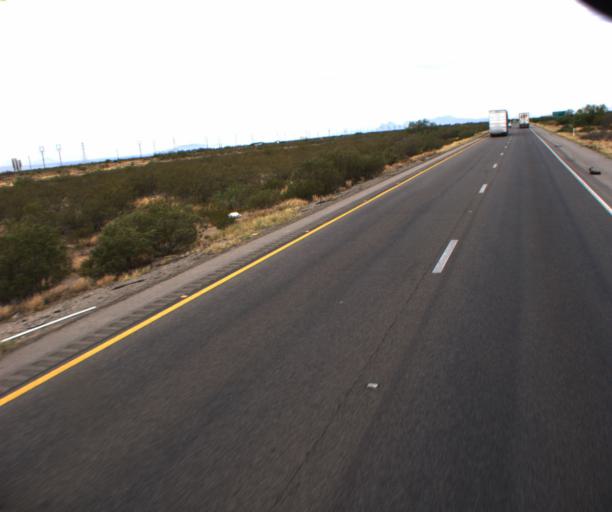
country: US
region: Arizona
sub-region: Pima County
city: Vail
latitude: 32.0359
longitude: -110.7308
